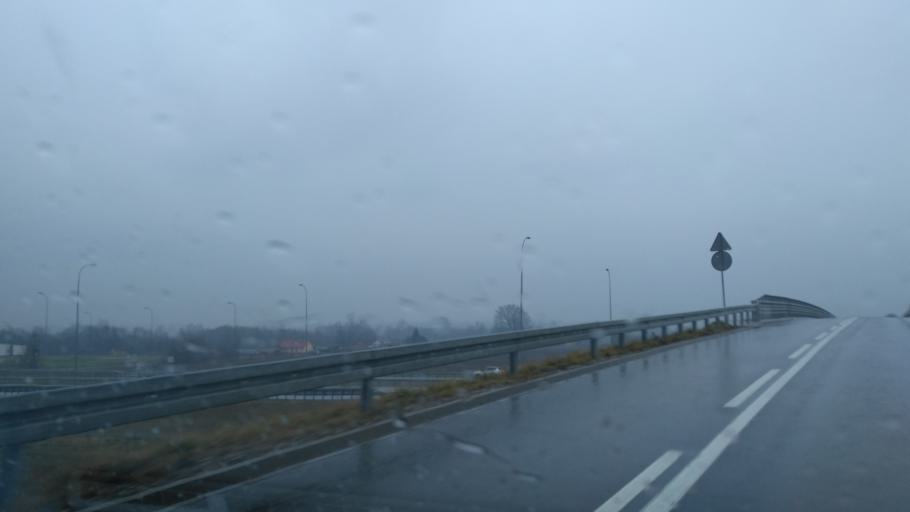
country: PL
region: Subcarpathian Voivodeship
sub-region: Powiat lancucki
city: Czarna
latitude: 50.0908
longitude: 22.1700
